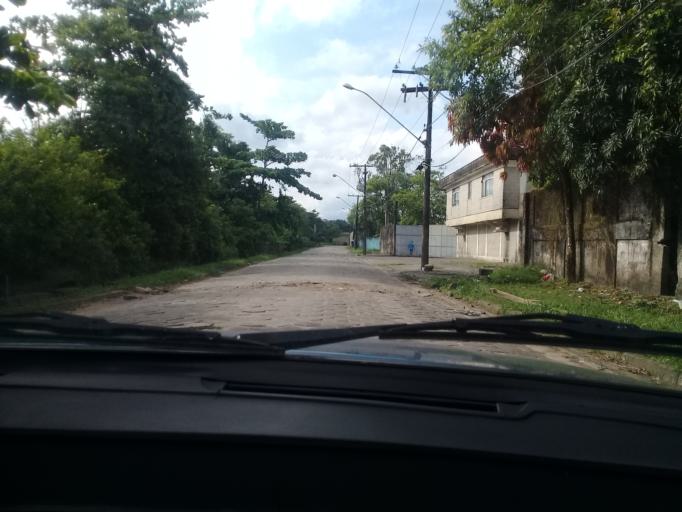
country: BR
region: Sao Paulo
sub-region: Guaruja
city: Guaruja
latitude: -23.9856
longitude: -46.2802
